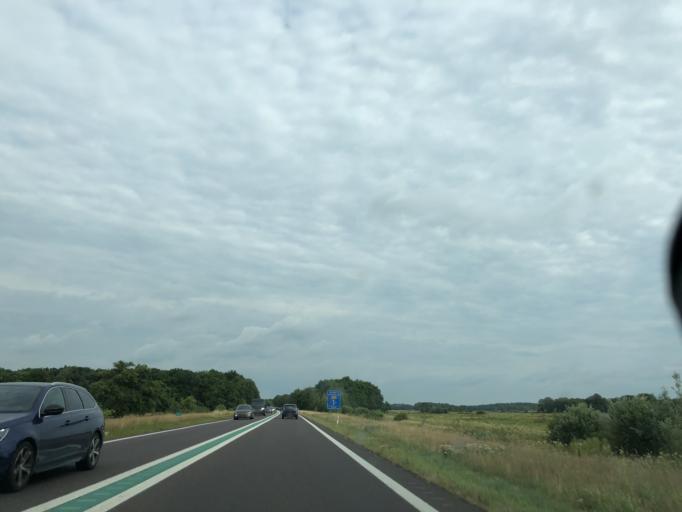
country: NL
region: Drenthe
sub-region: Gemeente Tynaarlo
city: Tynaarlo
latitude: 53.0915
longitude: 6.6426
